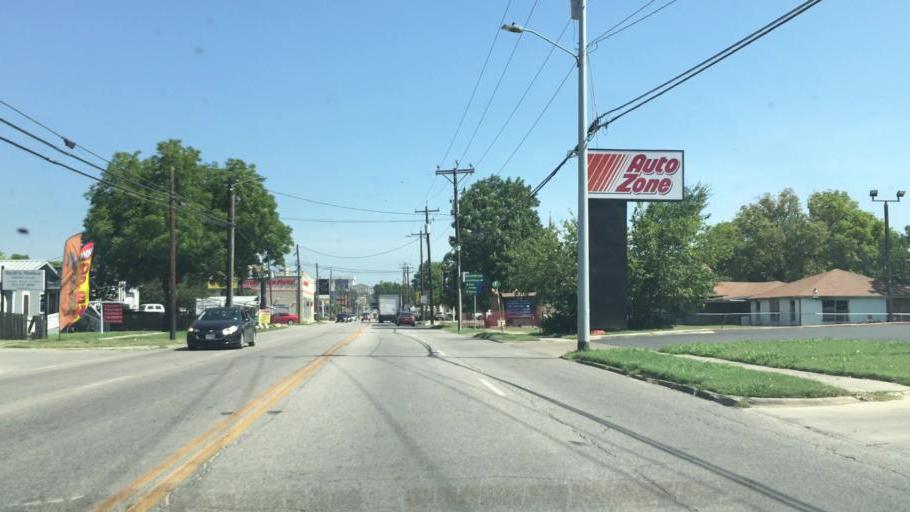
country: US
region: Texas
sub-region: Hays County
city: San Marcos
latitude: 29.8736
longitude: -97.9398
